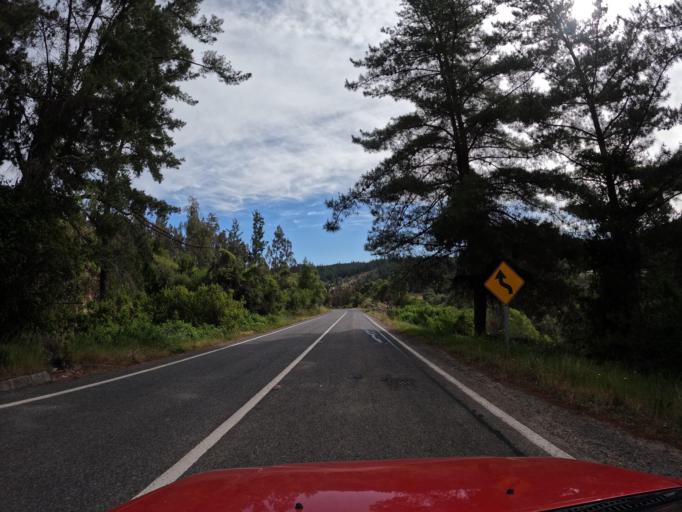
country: CL
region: Maule
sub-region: Provincia de Talca
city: Talca
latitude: -35.3021
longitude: -71.9629
